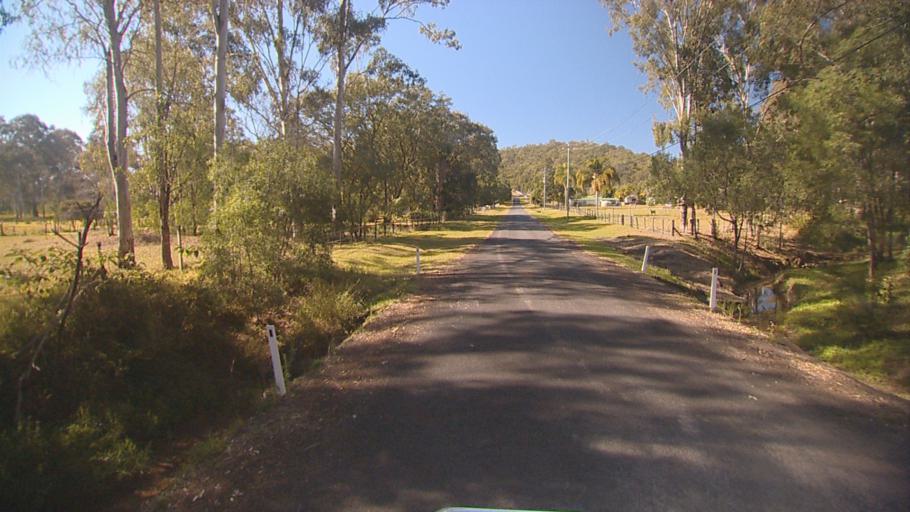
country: AU
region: Queensland
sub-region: Logan
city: Logan Reserve
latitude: -27.7651
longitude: 153.1401
